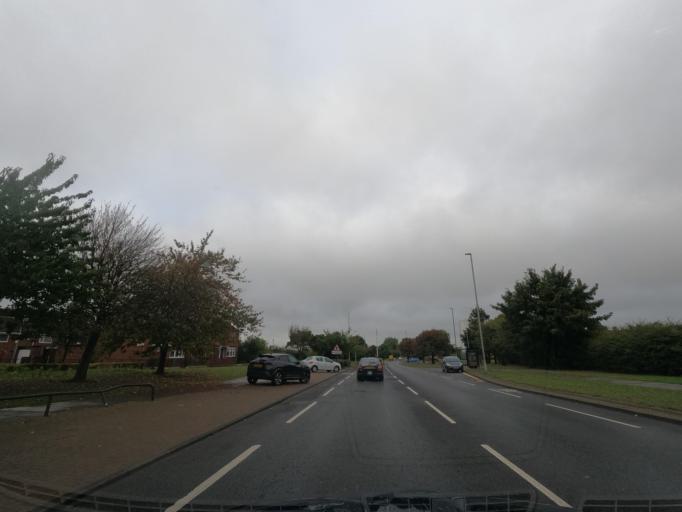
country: GB
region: England
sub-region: Middlesbrough
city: Nunthorpe
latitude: 54.5555
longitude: -1.1861
